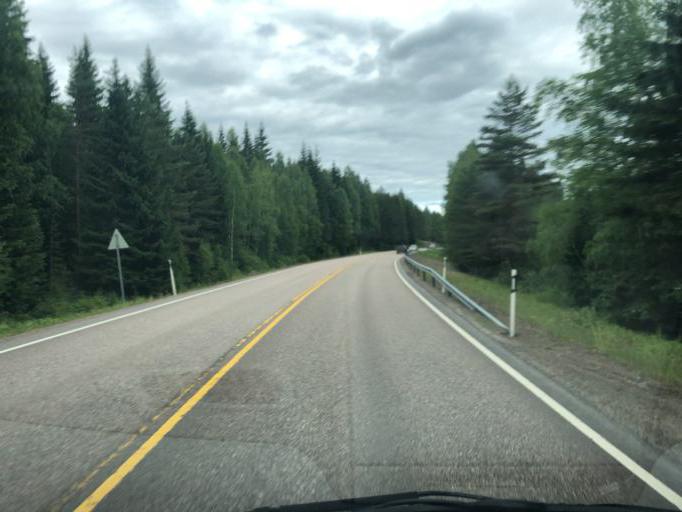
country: FI
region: Southern Savonia
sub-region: Mikkeli
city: Maentyharju
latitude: 61.1412
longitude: 27.1090
